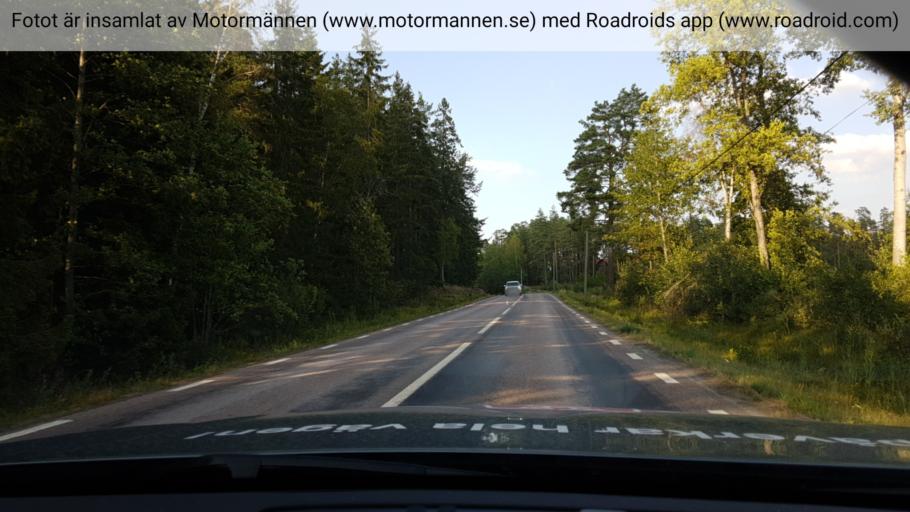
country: SE
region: Soedermanland
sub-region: Strangnas Kommun
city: Mariefred
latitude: 59.2309
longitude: 17.1698
